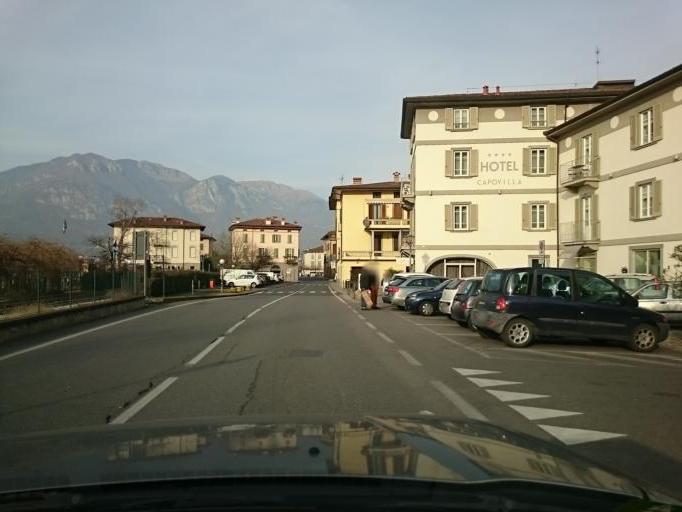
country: IT
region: Lombardy
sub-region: Provincia di Brescia
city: Pisogne
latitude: 45.8024
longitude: 10.1062
